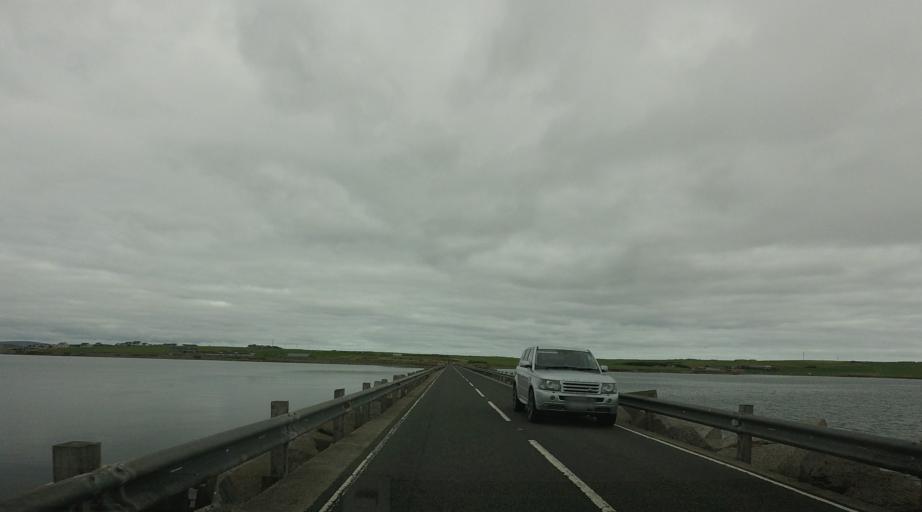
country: GB
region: Scotland
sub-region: Orkney Islands
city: Kirkwall
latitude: 58.8909
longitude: -2.8959
